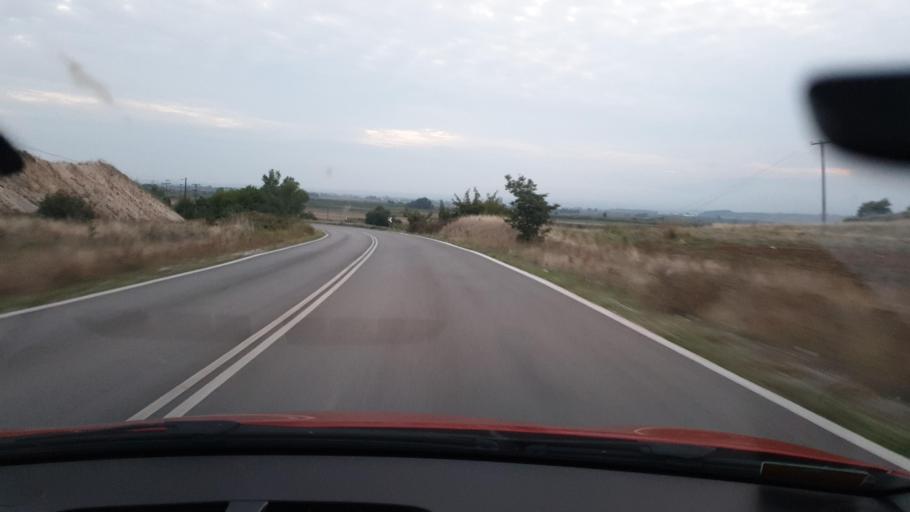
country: GR
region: Central Macedonia
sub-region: Nomos Kilkis
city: Polykastro
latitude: 41.0125
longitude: 22.6383
